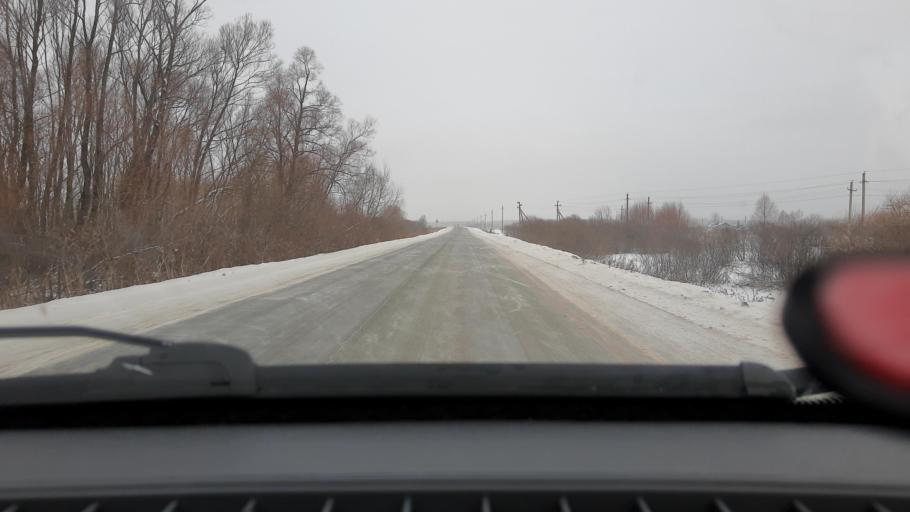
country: RU
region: Bashkortostan
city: Iglino
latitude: 54.7422
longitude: 56.3974
